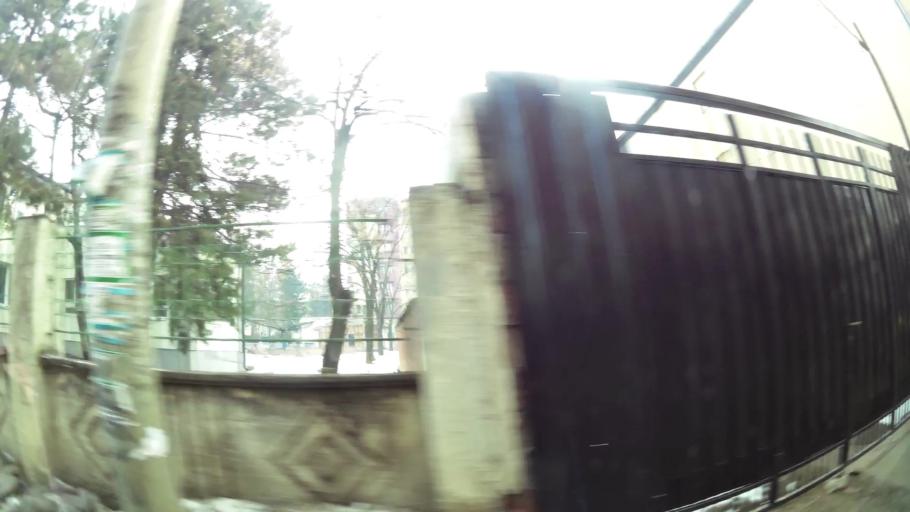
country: XK
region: Pristina
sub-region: Komuna e Prishtines
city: Pristina
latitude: 42.6664
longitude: 21.1708
